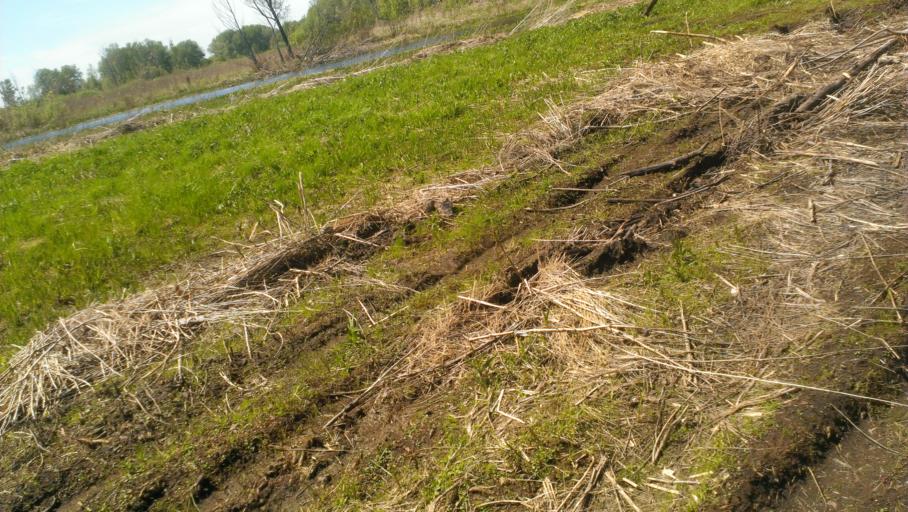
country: RU
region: Altai Krai
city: Zaton
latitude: 53.3186
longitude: 83.8830
